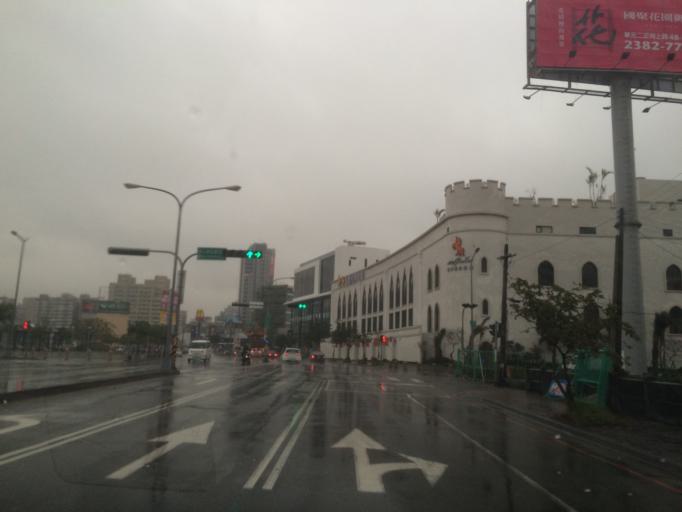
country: TW
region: Taiwan
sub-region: Taichung City
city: Taichung
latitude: 24.1449
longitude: 120.6303
